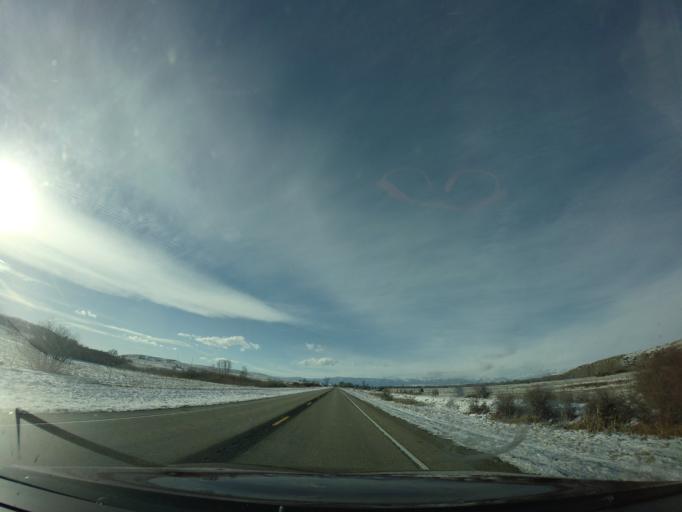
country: US
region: Montana
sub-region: Stillwater County
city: Columbus
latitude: 45.4187
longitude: -109.1107
